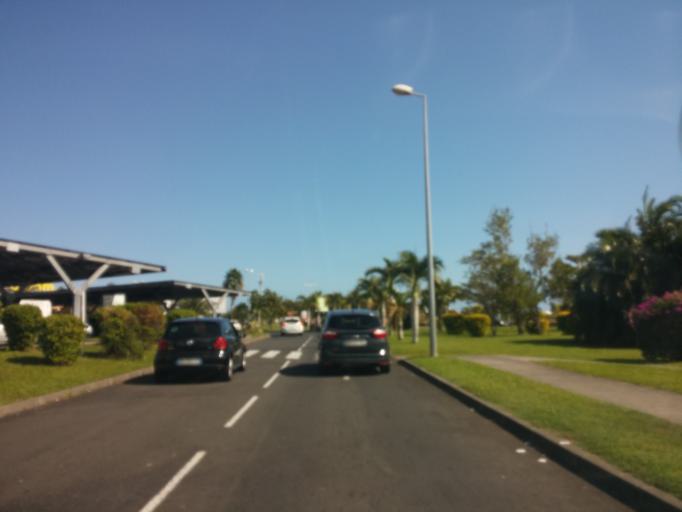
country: RE
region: Reunion
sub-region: Reunion
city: Le Port
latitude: -20.9546
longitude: 55.3090
